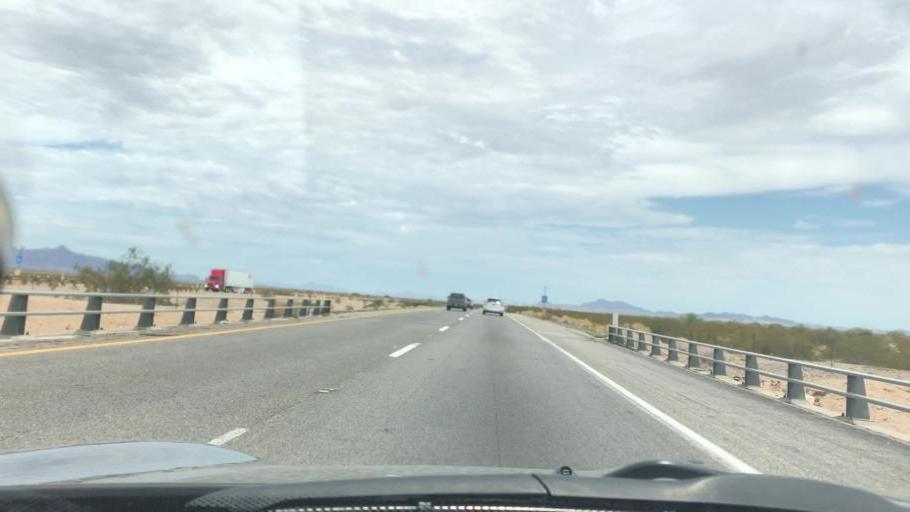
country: US
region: California
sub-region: Riverside County
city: Mesa Verde
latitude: 33.6212
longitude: -115.0387
